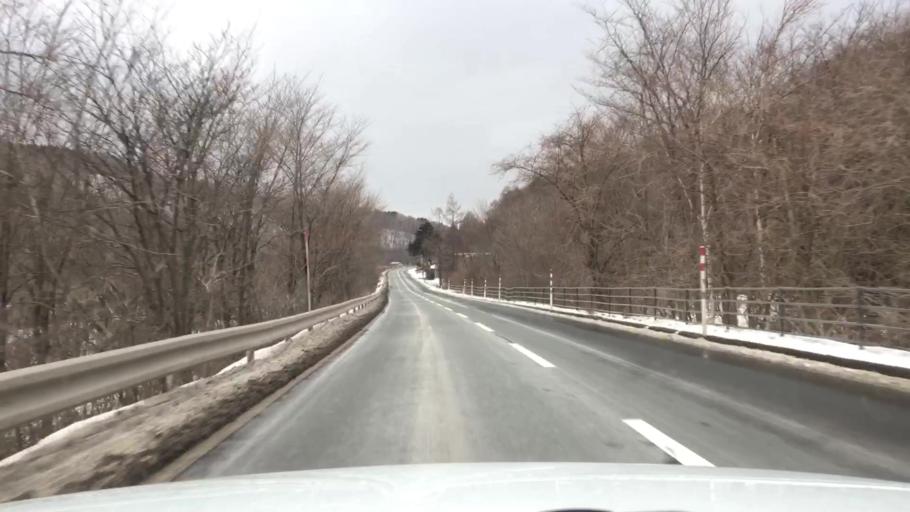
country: JP
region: Iwate
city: Morioka-shi
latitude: 39.6374
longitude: 141.4337
